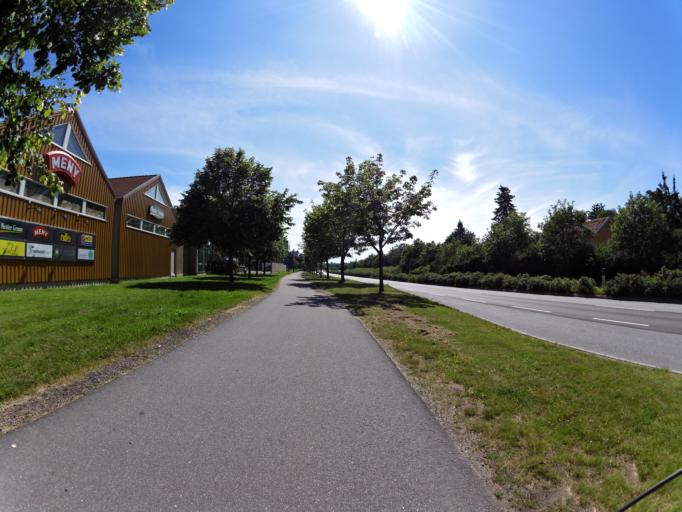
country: NO
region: Ostfold
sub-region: Fredrikstad
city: Fredrikstad
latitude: 59.2252
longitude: 10.9536
